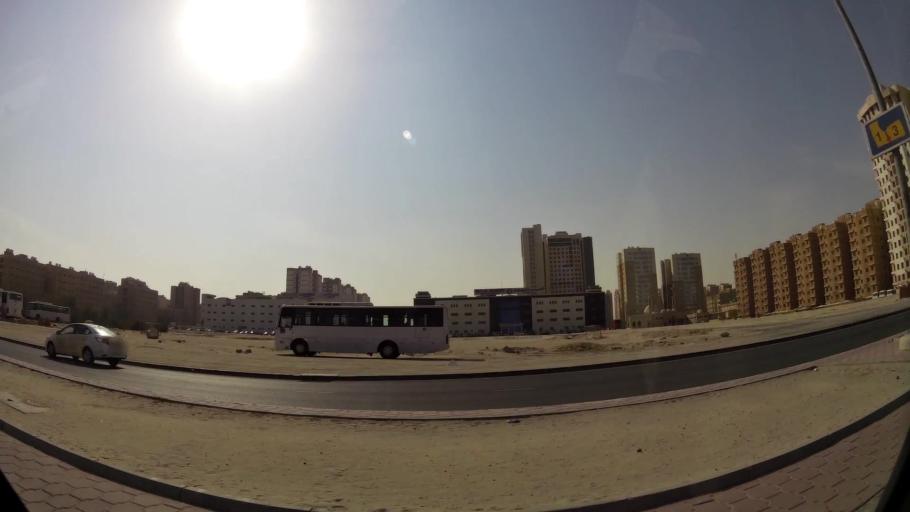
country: KW
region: Al Ahmadi
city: Al Mahbulah
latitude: 29.1426
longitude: 48.1204
